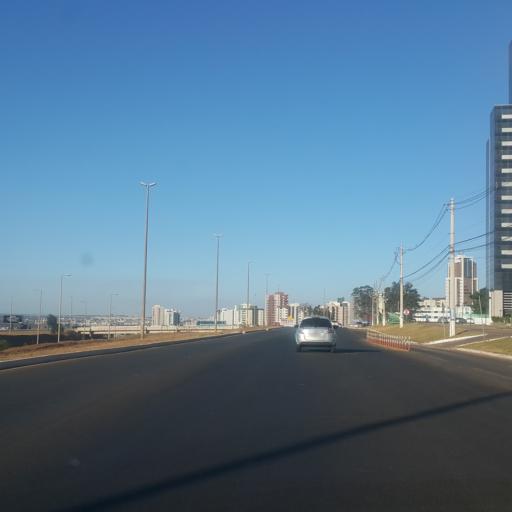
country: BR
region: Federal District
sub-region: Brasilia
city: Brasilia
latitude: -15.8312
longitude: -48.0420
